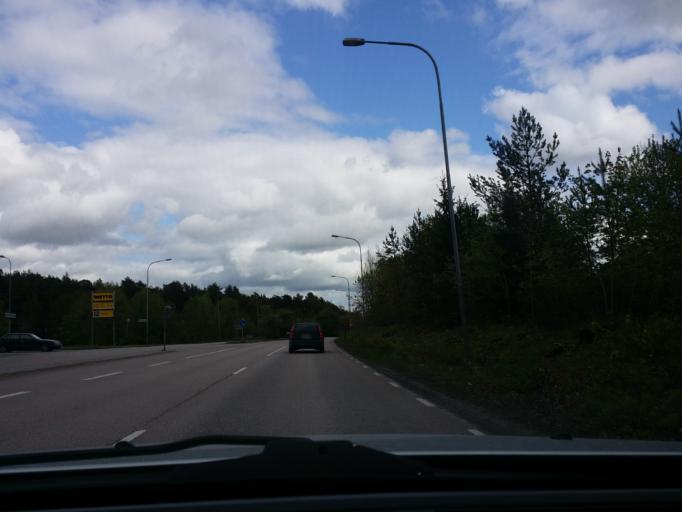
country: SE
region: Vaestmanland
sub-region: Vasteras
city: Vasteras
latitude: 59.6091
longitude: 16.5093
